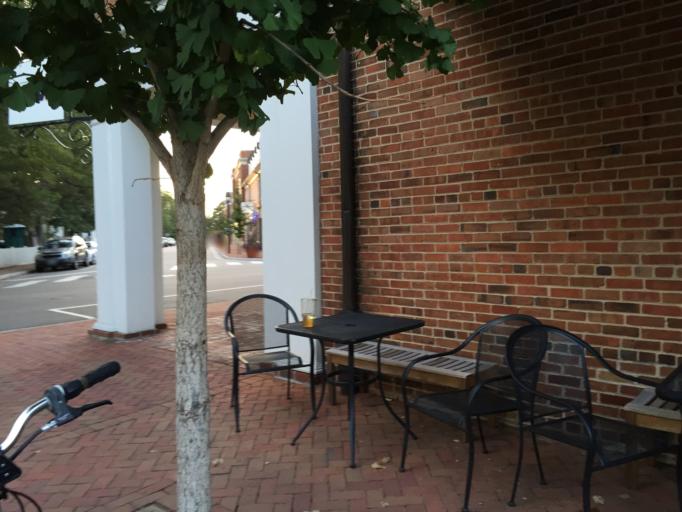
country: US
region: Virginia
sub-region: City of Williamsburg
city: Williamsburg
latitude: 37.2722
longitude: -76.7074
